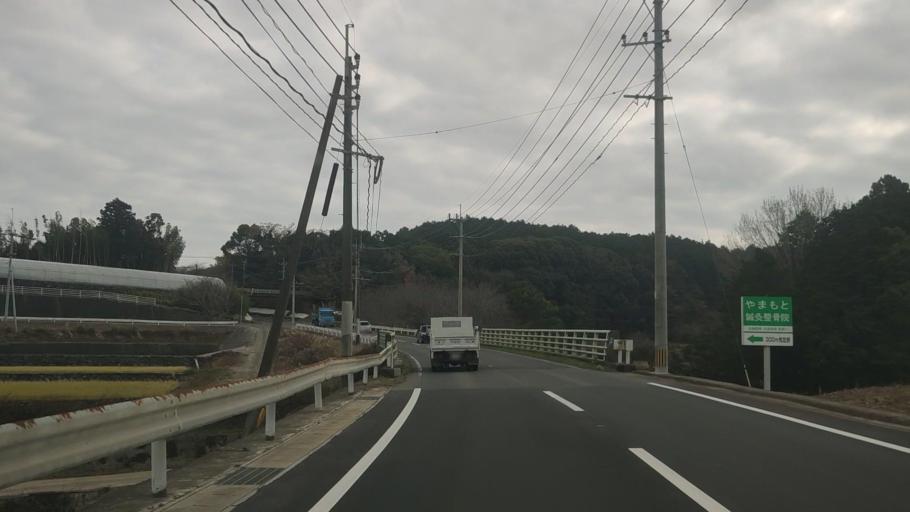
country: JP
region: Nagasaki
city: Shimabara
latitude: 32.8491
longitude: 130.2774
